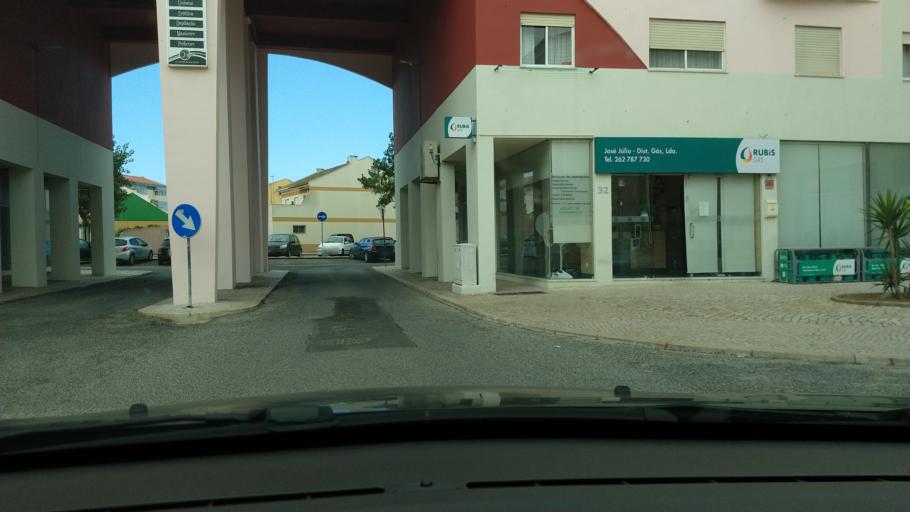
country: PT
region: Leiria
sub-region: Peniche
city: Peniche
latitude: 39.3623
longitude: -9.3905
